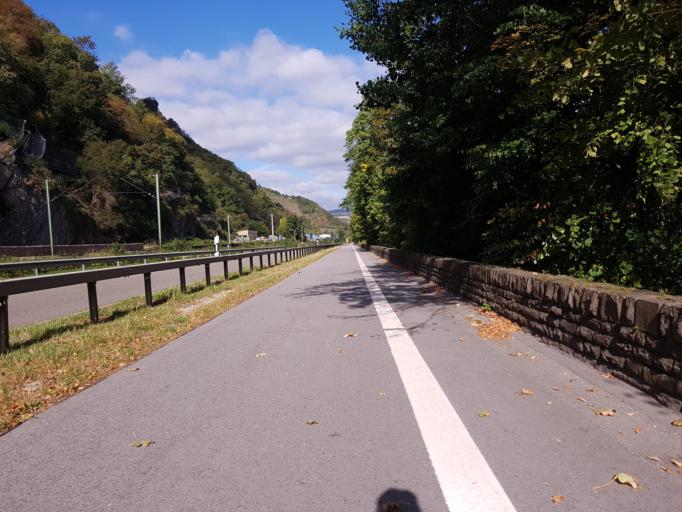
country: DE
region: Rheinland-Pfalz
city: Kaub
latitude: 50.0902
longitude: 7.7517
